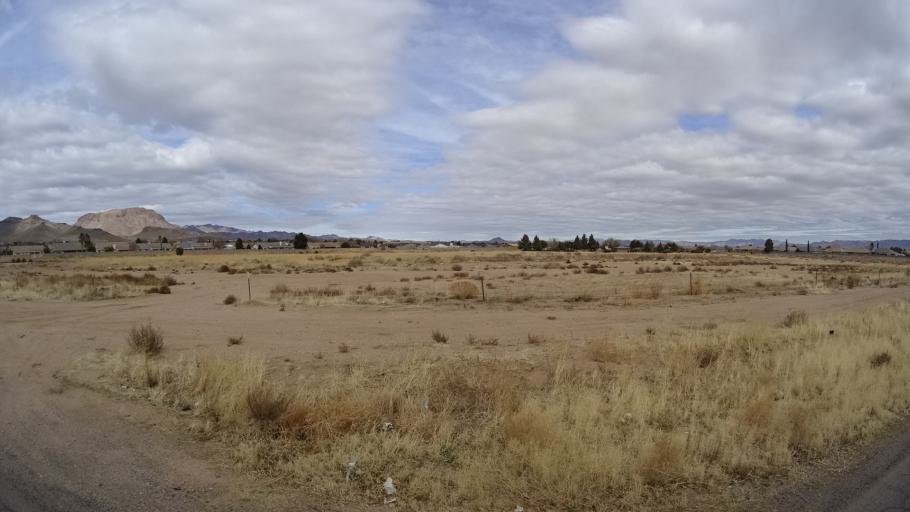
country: US
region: Arizona
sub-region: Mohave County
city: New Kingman-Butler
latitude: 35.2325
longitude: -114.0267
